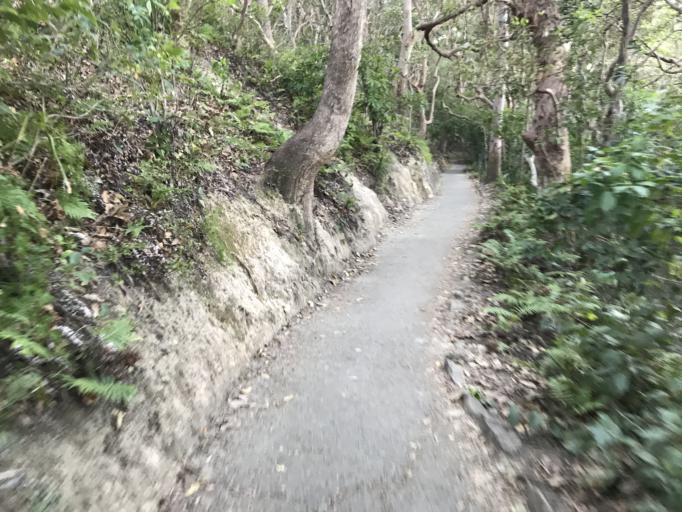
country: AU
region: Queensland
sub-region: Gold Coast
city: Palm Beach
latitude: -28.0967
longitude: 153.4567
